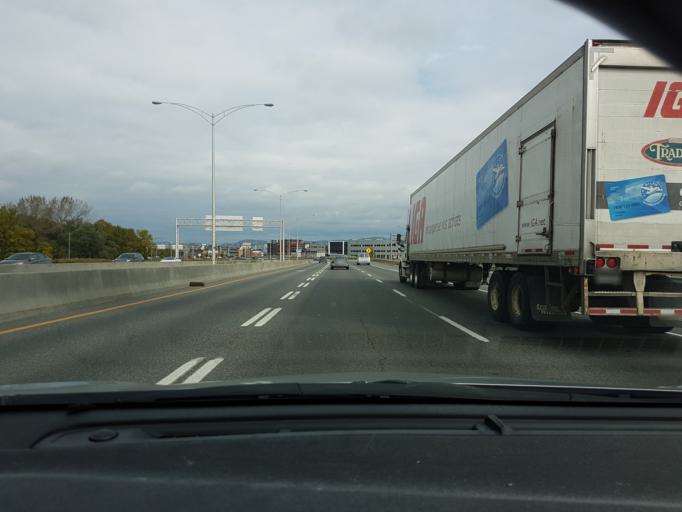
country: CA
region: Quebec
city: L'Ancienne-Lorette
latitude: 46.8116
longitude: -71.2890
